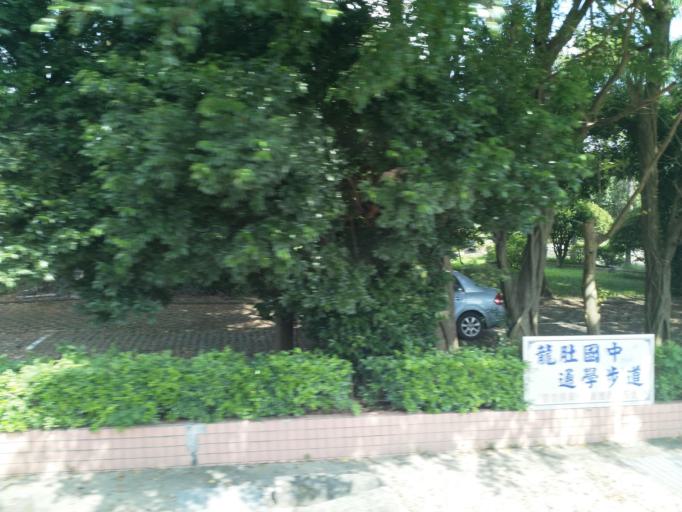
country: TW
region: Taiwan
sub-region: Pingtung
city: Pingtung
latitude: 22.8779
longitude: 120.5708
